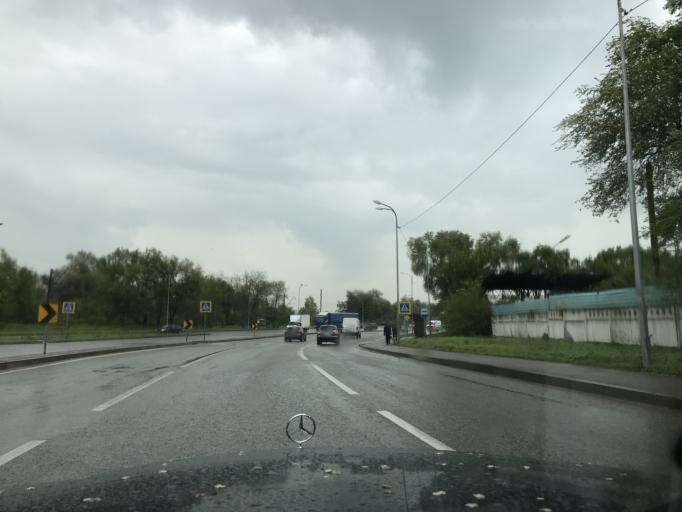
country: KZ
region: Almaty Oblysy
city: Pervomayskiy
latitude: 43.3326
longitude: 76.9605
